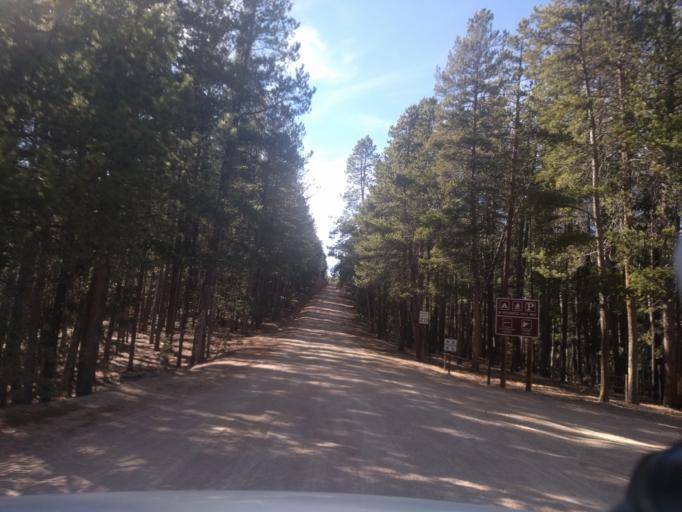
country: US
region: Colorado
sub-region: Douglas County
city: Perry Park
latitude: 39.2192
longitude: -105.0646
